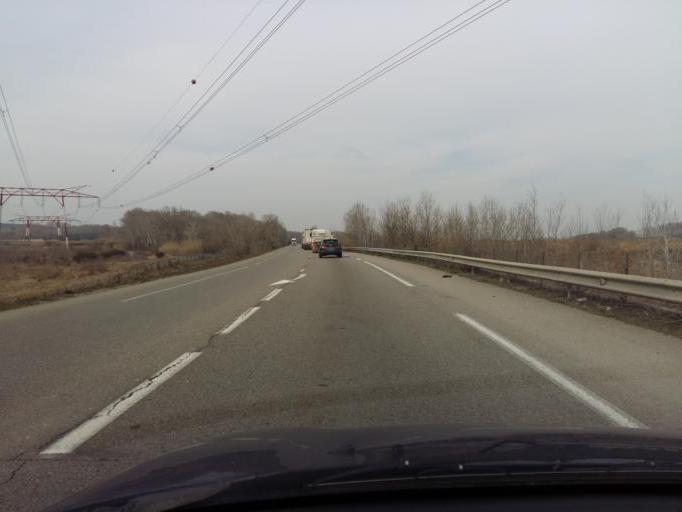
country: FR
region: Provence-Alpes-Cote d'Azur
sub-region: Departement des Bouches-du-Rhone
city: Noves
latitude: 43.8861
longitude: 4.9110
